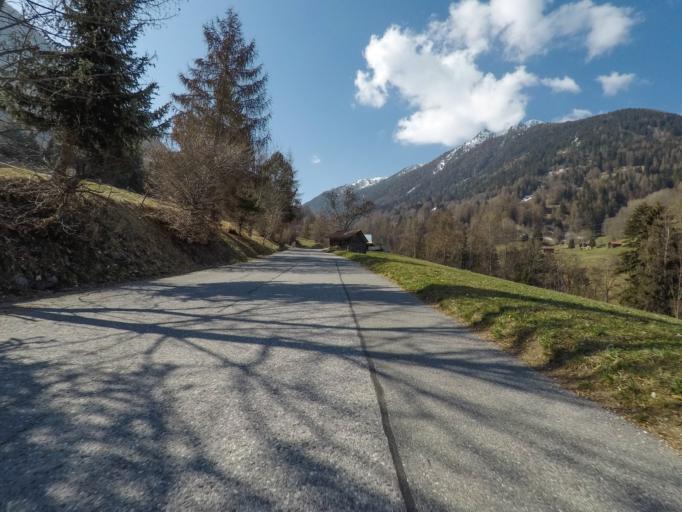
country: CH
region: Valais
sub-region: Conthey District
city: Basse-Nendaz
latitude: 46.1718
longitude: 7.3222
